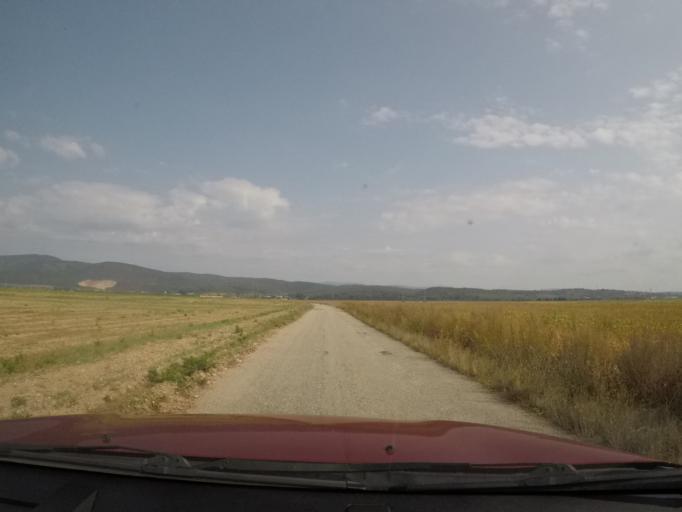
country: SK
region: Kosicky
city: Moldava nad Bodvou
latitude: 48.5911
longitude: 20.9570
